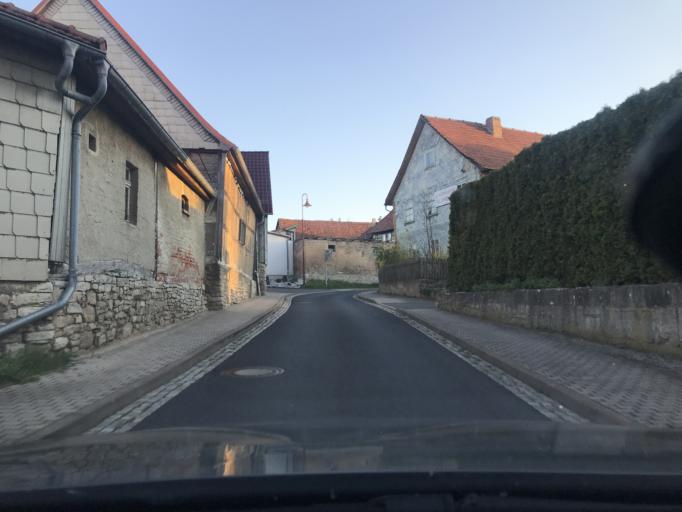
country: DE
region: Thuringia
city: Sollstedt
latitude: 51.2715
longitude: 10.5115
